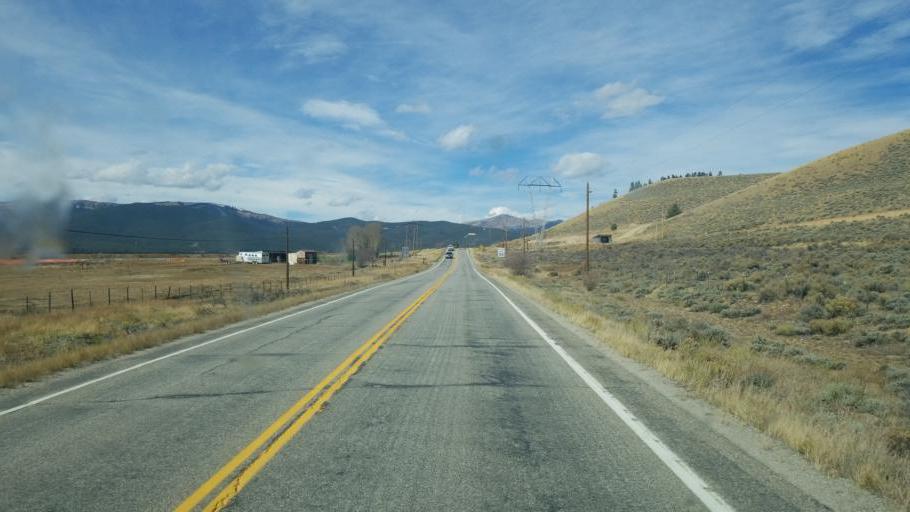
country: US
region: Colorado
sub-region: Lake County
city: Leadville North
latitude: 39.1999
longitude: -106.3407
